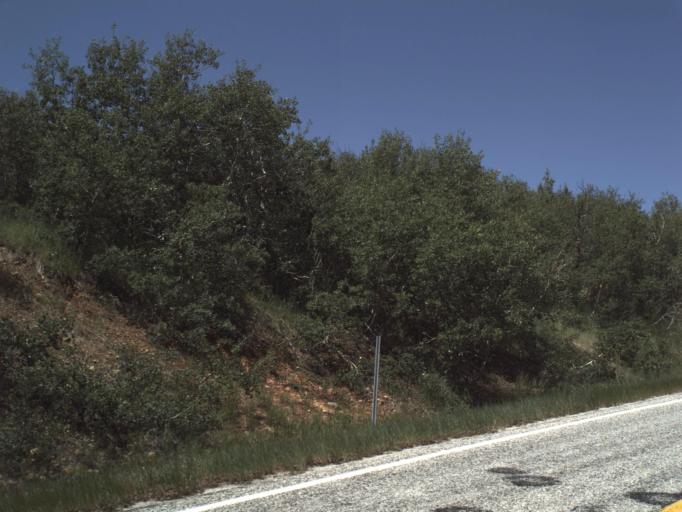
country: US
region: Utah
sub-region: Weber County
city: Wolf Creek
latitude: 41.4142
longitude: -111.5788
